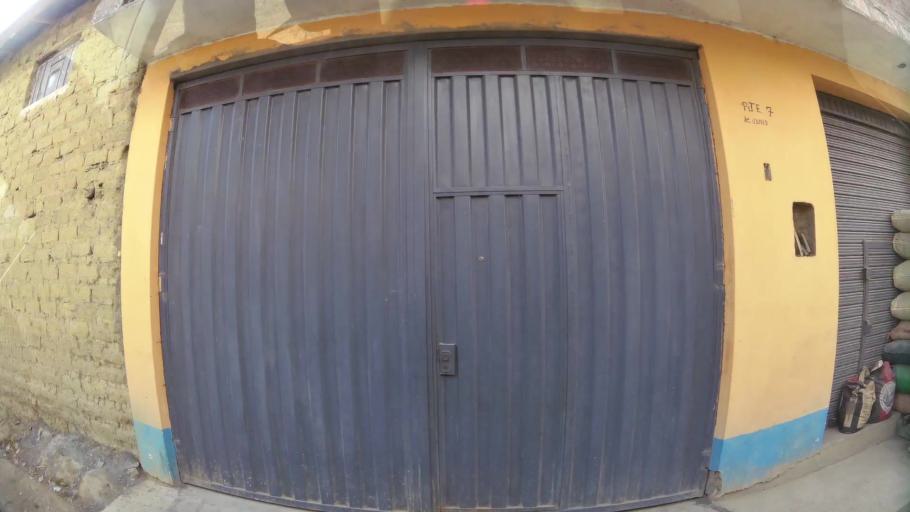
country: PE
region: Junin
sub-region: Provincia de Huancayo
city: Huancayo
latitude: -12.0957
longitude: -75.2041
